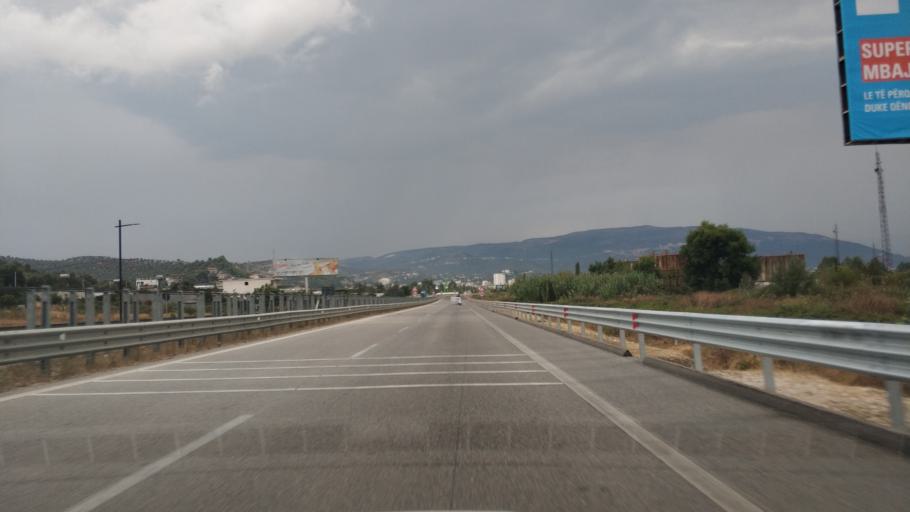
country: AL
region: Vlore
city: Vlore
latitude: 40.4891
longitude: 19.4750
